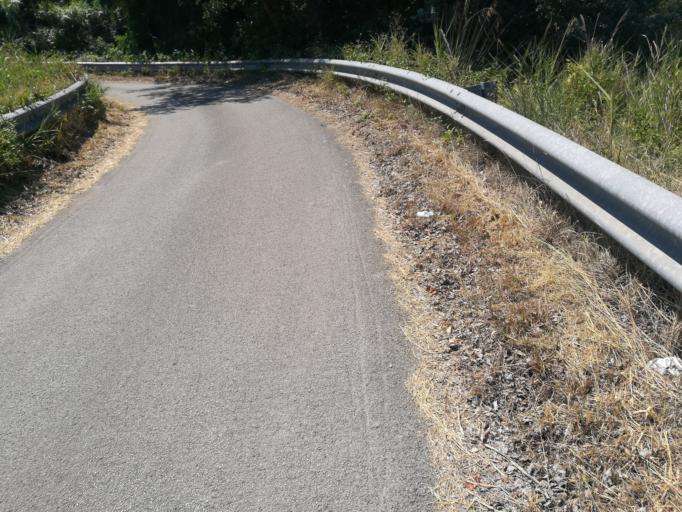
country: IT
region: Abruzzo
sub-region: Provincia di Chieti
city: Ortona
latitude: 42.3428
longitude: 14.4114
